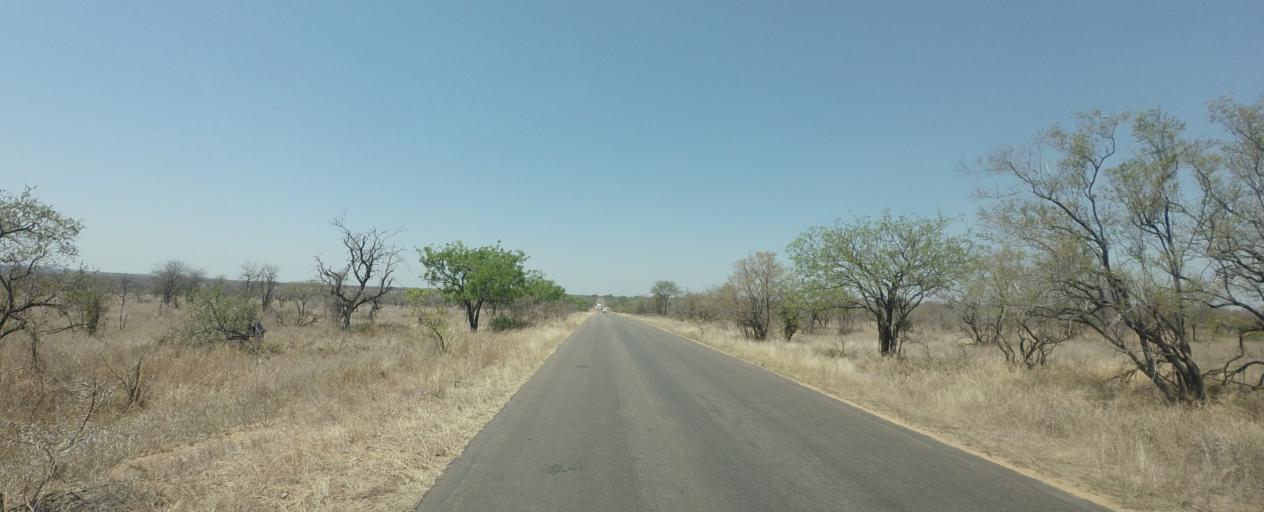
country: ZA
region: Limpopo
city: Thulamahashi
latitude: -24.4731
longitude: 31.4098
